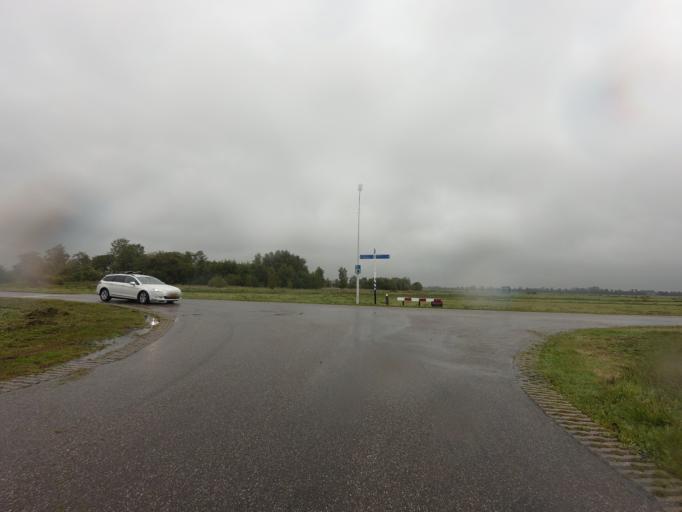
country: NL
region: Friesland
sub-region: Gemeente Tytsjerksteradiel
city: Garyp
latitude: 53.1314
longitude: 5.9588
